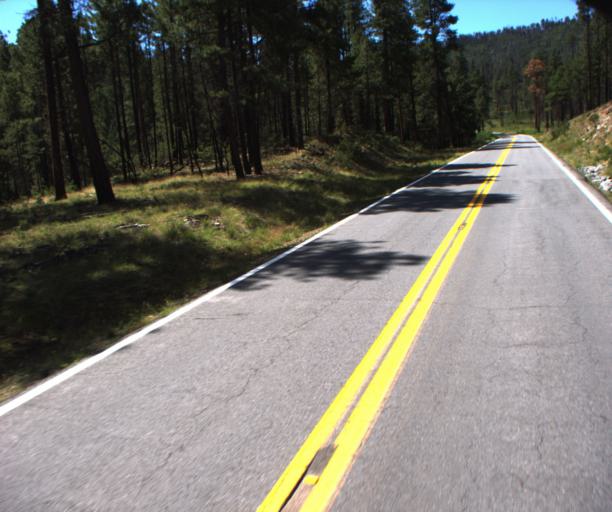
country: US
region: Arizona
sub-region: Apache County
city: Eagar
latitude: 33.7398
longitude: -109.2075
